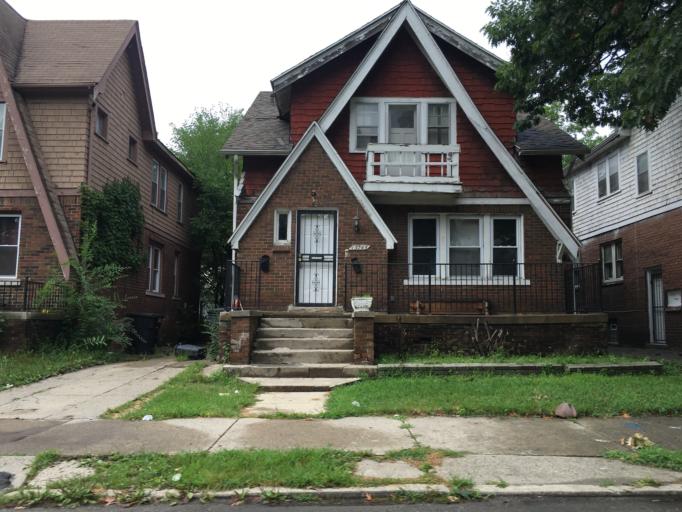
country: US
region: Michigan
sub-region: Oakland County
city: Ferndale
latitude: 42.4069
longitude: -83.1545
